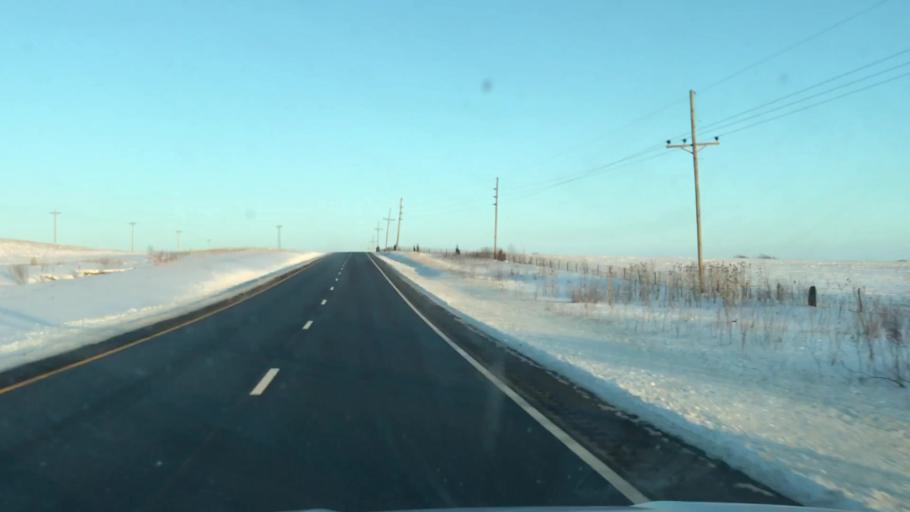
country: US
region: Missouri
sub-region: Clinton County
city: Cameron
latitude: 39.7544
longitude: -94.2950
